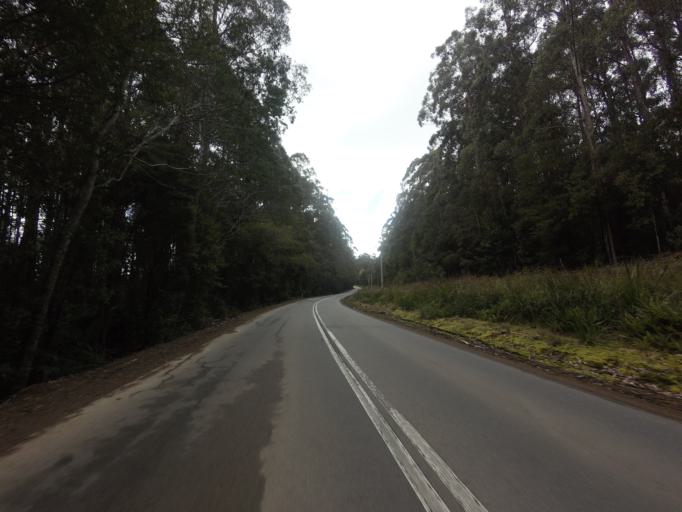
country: AU
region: Tasmania
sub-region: Huon Valley
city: Geeveston
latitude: -43.3855
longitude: 146.9616
